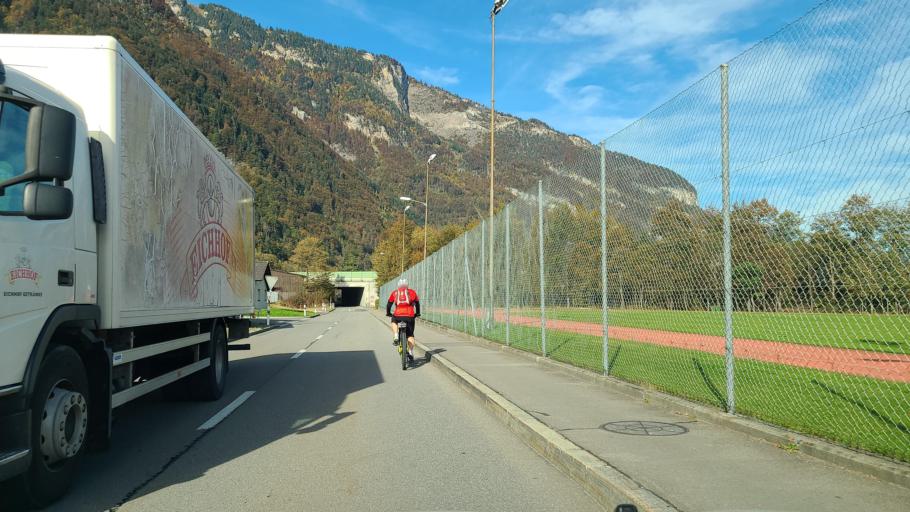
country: CH
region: Uri
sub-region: Uri
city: Seedorf
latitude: 46.8868
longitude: 8.6045
